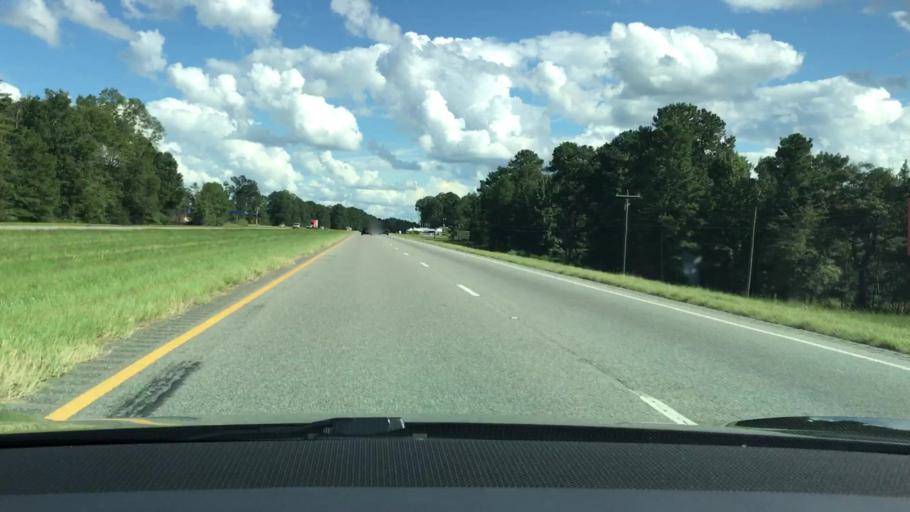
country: US
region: Alabama
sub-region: Montgomery County
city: Taylor
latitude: 32.0480
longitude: -86.0402
